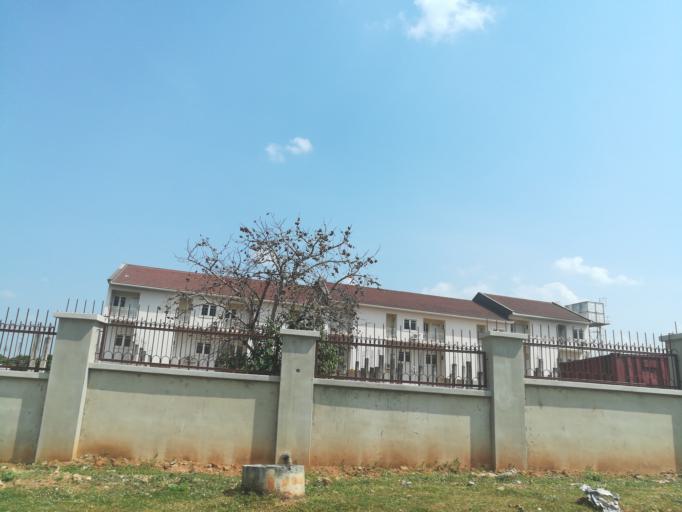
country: NG
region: Abuja Federal Capital Territory
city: Abuja
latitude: 9.0539
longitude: 7.4456
